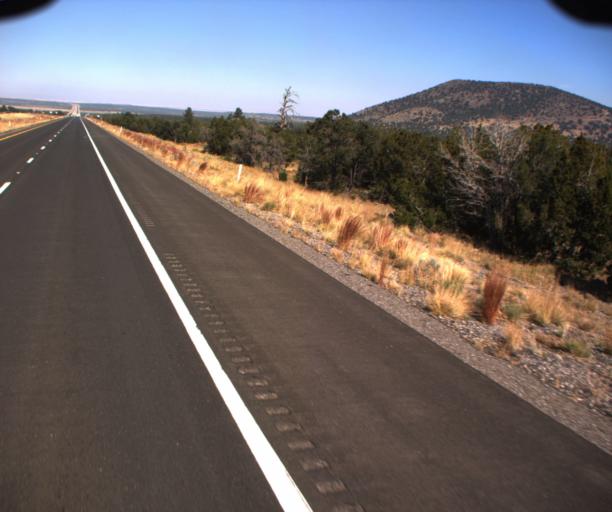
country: US
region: Arizona
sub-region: Coconino County
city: Flagstaff
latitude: 35.4016
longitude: -111.5756
